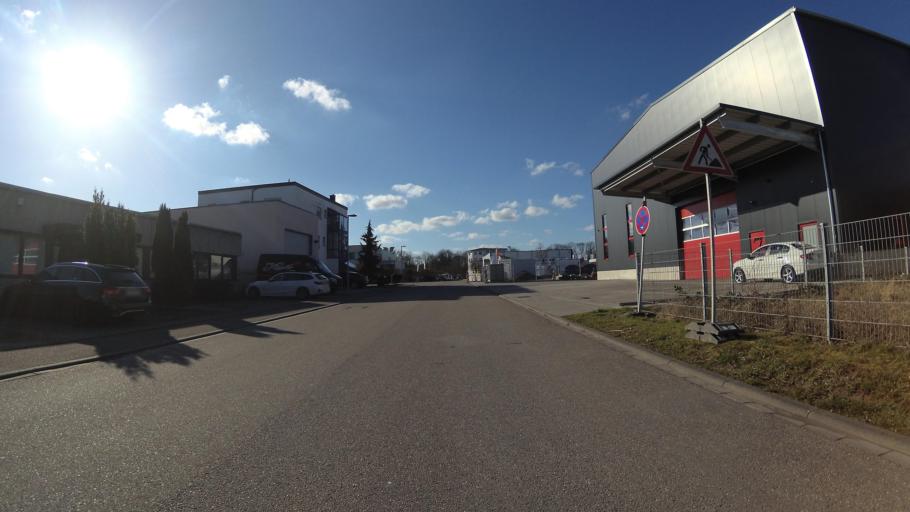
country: DE
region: Baden-Wuerttemberg
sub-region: Regierungsbezirk Stuttgart
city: Untereisesheim
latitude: 49.2382
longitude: 9.2182
